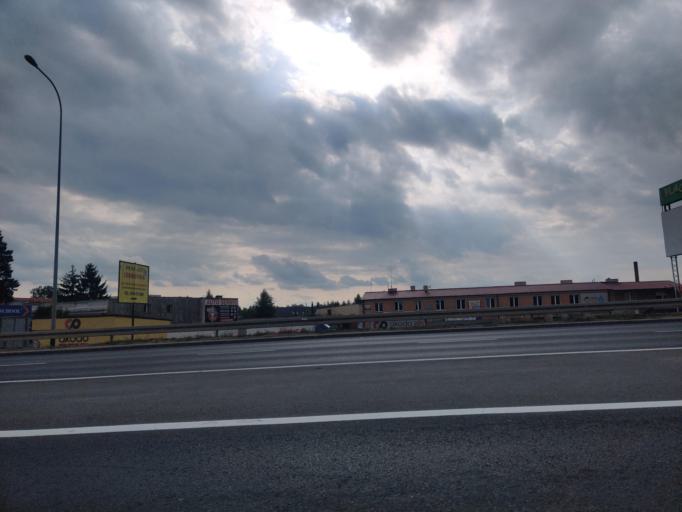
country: PL
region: Greater Poland Voivodeship
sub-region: Konin
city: Konin
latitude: 52.2190
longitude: 18.2528
